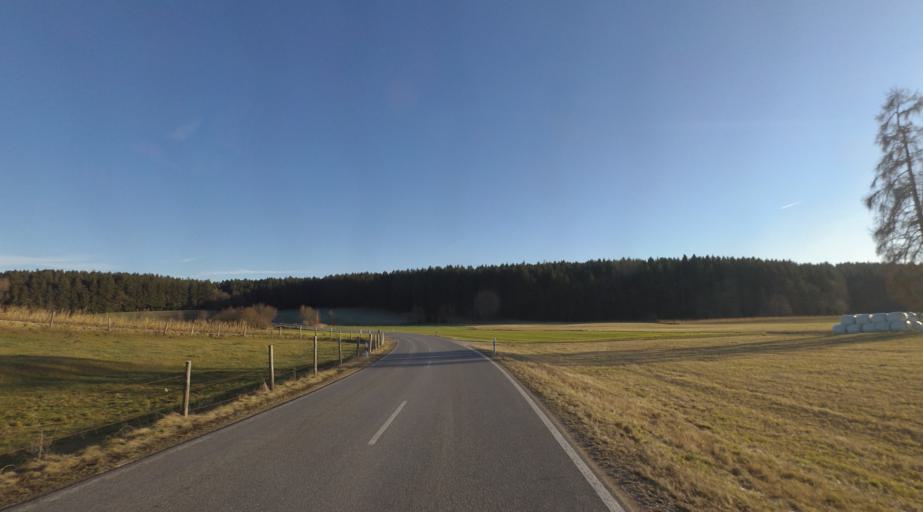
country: DE
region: Bavaria
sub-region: Upper Bavaria
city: Trostberg an der Alz
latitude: 48.0194
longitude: 12.5923
